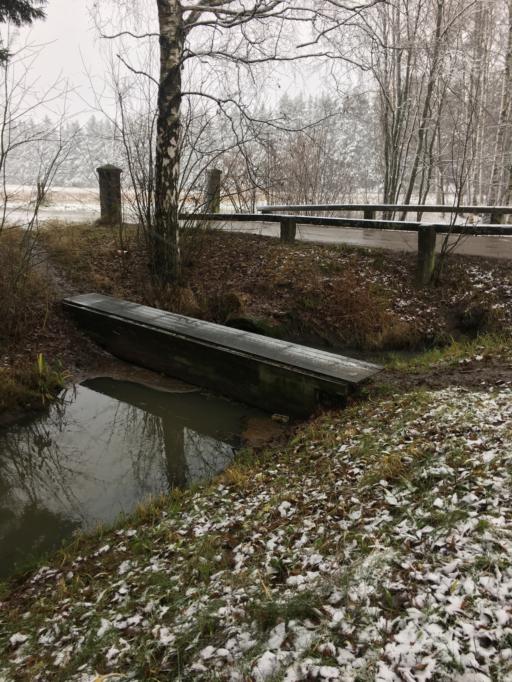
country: FI
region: Uusimaa
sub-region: Helsinki
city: Vantaa
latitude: 60.2603
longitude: 25.0327
